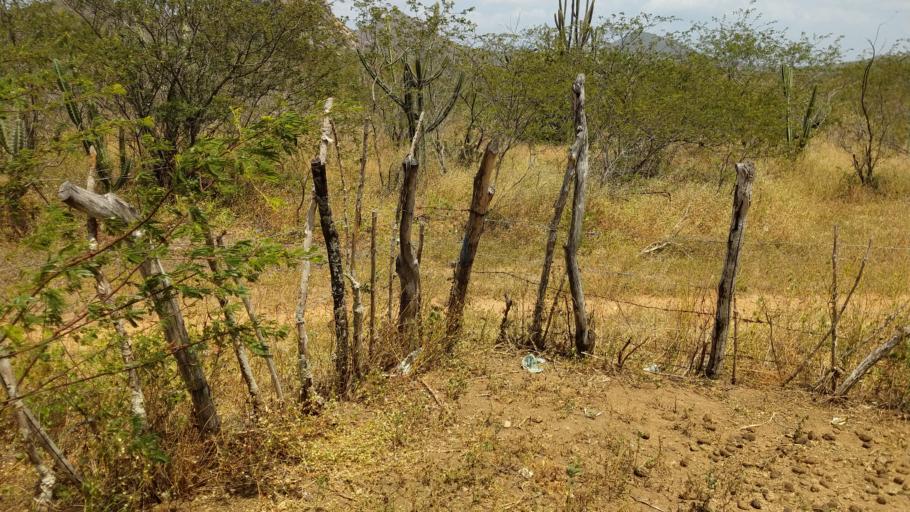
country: BR
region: Rio Grande do Norte
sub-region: Sao Tome
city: Sao Tome
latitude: -5.9690
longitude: -35.9106
